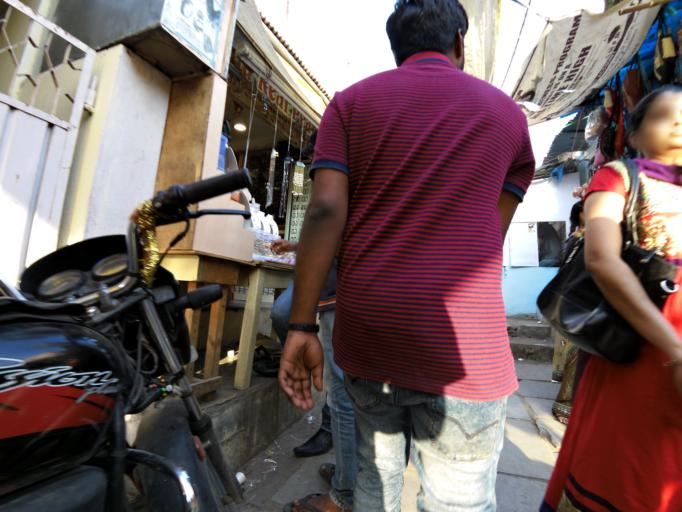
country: IN
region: Telangana
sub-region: Hyderabad
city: Hyderabad
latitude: 17.4051
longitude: 78.4684
